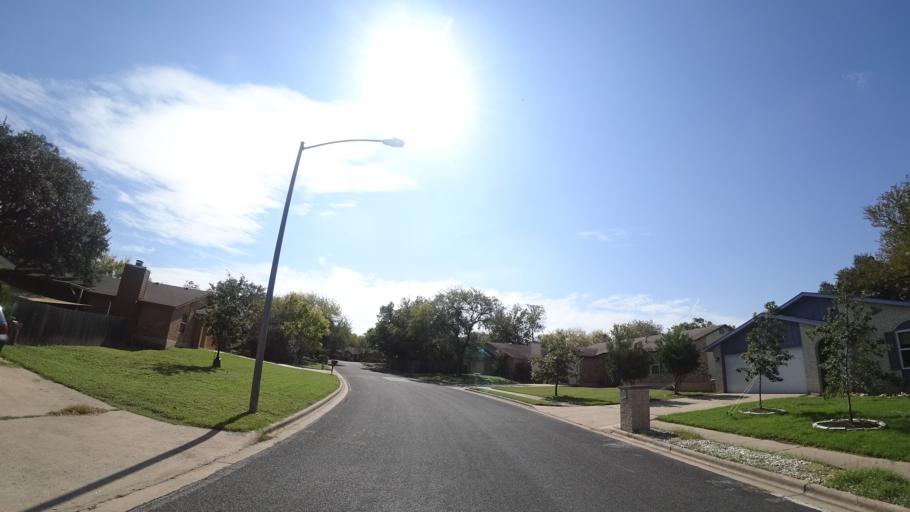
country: US
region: Texas
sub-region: Travis County
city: Shady Hollow
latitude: 30.2128
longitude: -97.8244
